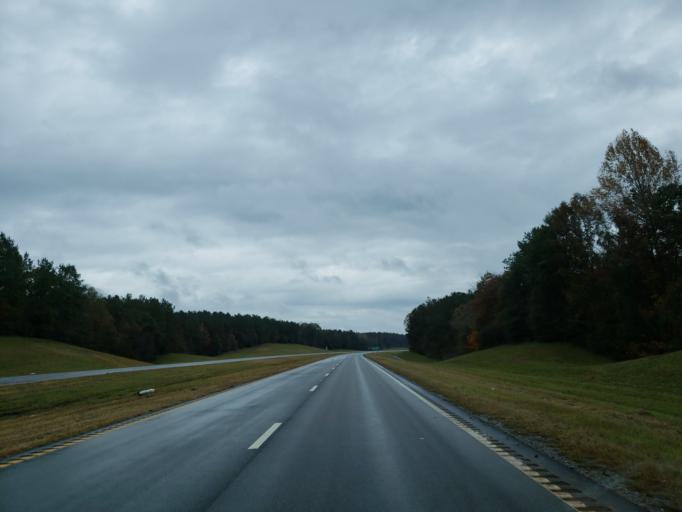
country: US
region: Mississippi
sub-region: Wayne County
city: Waynesboro
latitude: 31.6984
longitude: -88.6576
